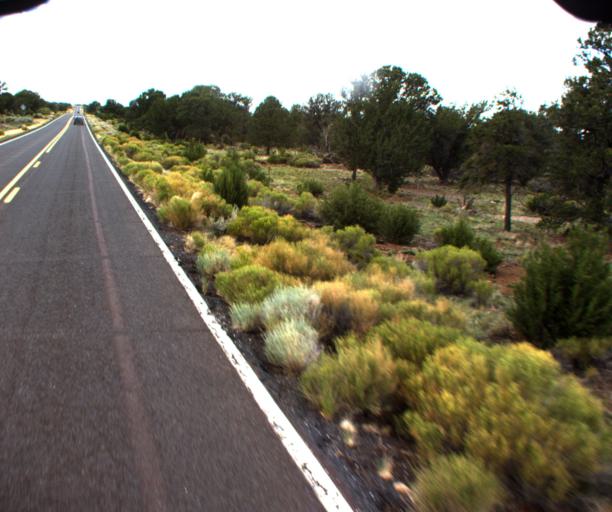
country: US
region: Arizona
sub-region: Coconino County
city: Parks
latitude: 35.5455
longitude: -111.8582
